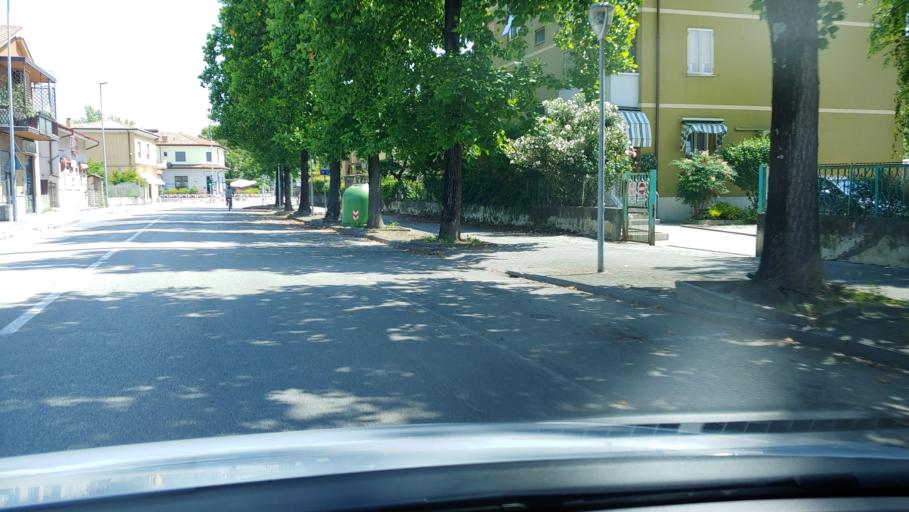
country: IT
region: Friuli Venezia Giulia
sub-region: Provincia di Gorizia
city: Staranzano
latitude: 45.8078
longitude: 13.5202
